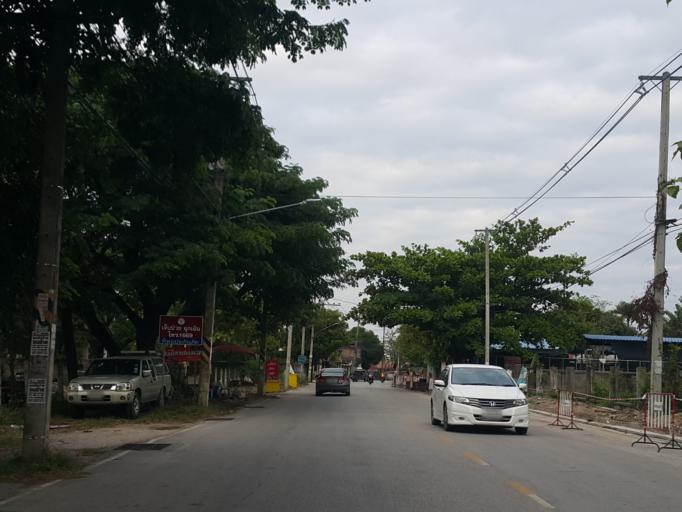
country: TH
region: Lampang
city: Lampang
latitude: 18.3002
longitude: 99.5054
